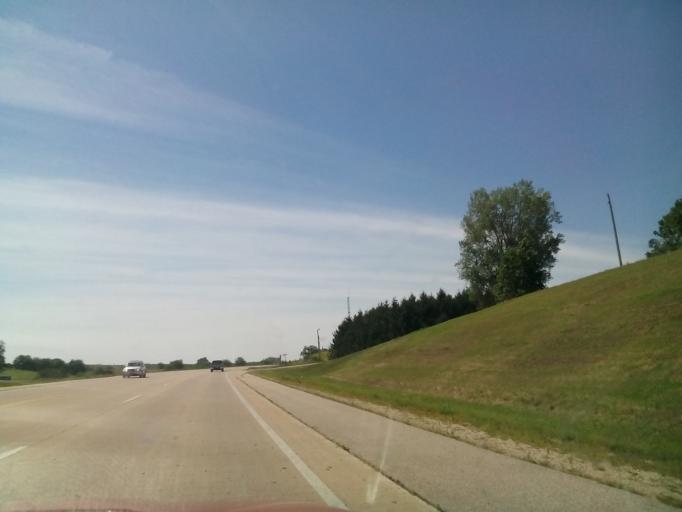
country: US
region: Wisconsin
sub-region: Green County
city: Monroe
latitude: 42.6303
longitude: -89.6322
